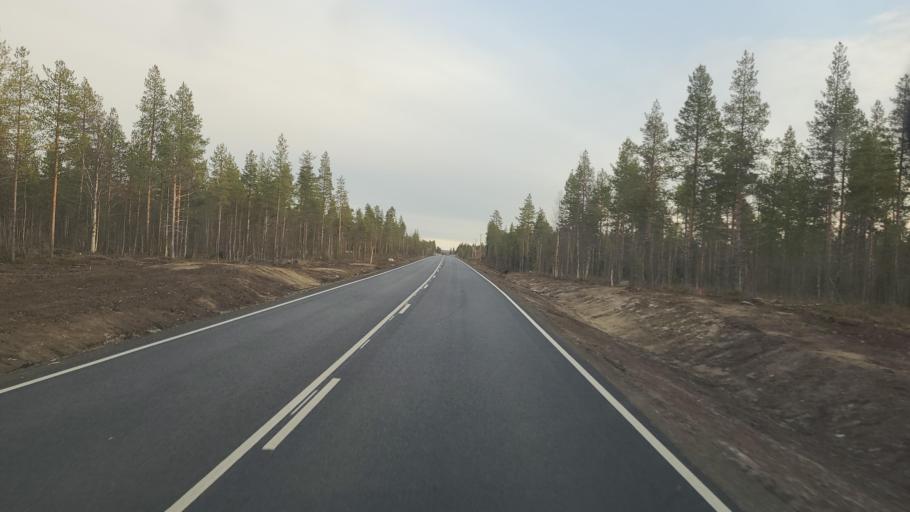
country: FI
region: Lapland
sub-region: Tunturi-Lappi
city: Kittilae
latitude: 67.8716
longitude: 24.9032
